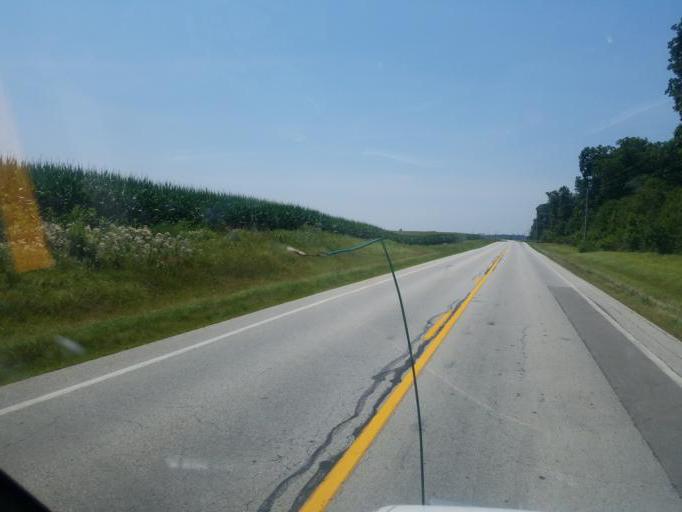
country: US
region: Ohio
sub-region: Shelby County
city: Fort Loramie
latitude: 40.3490
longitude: -84.3886
